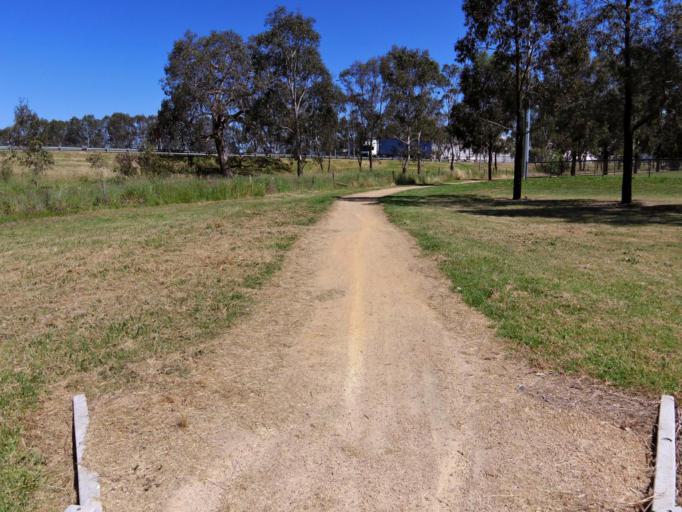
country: AU
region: Victoria
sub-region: Casey
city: Hampton Park
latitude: -38.0244
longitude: 145.2486
